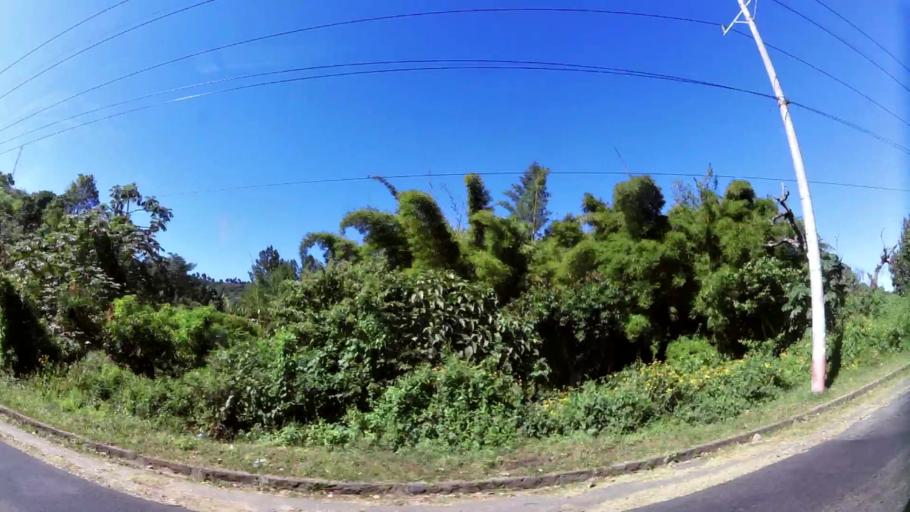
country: SV
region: Ahuachapan
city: Concepcion de Ataco
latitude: 13.8657
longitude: -89.8391
